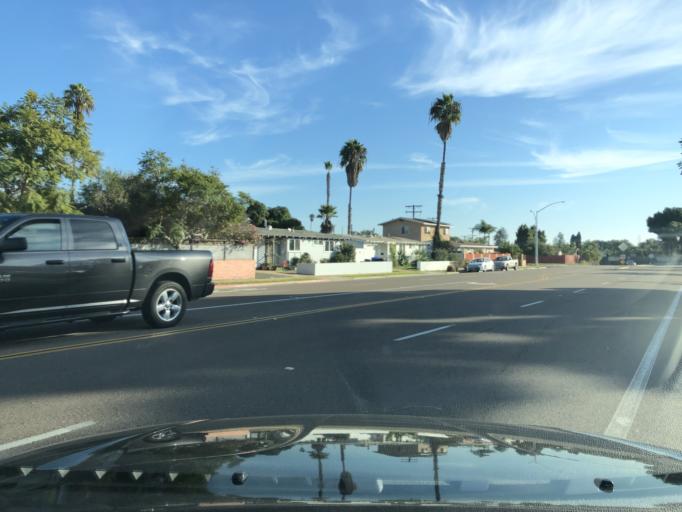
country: US
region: California
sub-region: San Diego County
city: La Jolla
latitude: 32.8329
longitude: -117.1950
